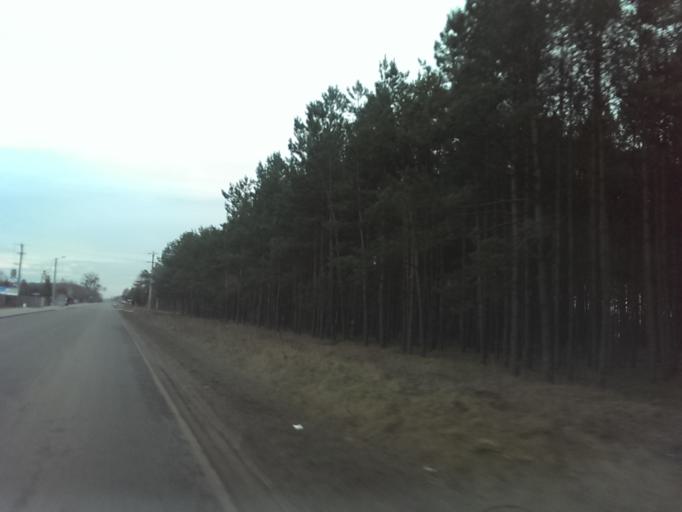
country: PL
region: Kujawsko-Pomorskie
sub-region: Powiat nakielski
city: Szubin
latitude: 53.0767
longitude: 17.7974
